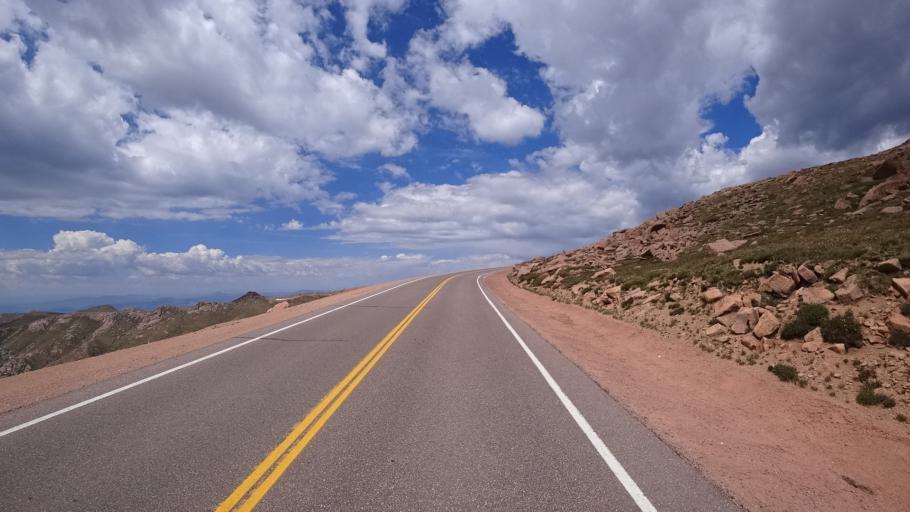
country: US
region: Colorado
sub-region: El Paso County
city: Cascade-Chipita Park
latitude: 38.8577
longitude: -105.0657
